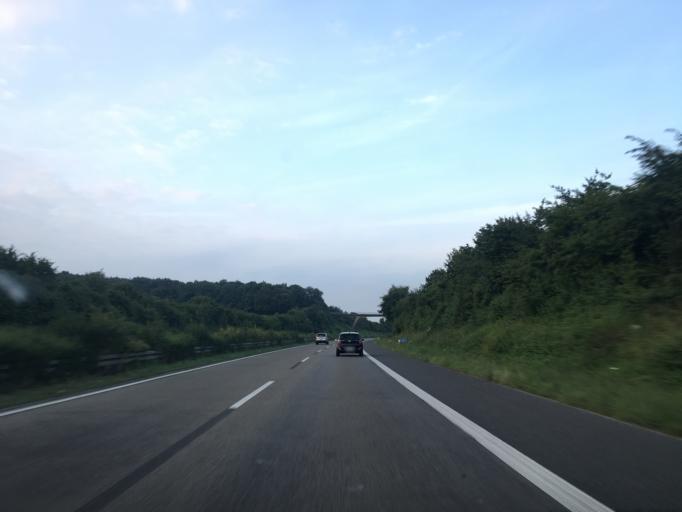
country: DE
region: North Rhine-Westphalia
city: Huckelhoven
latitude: 51.0653
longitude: 6.2041
